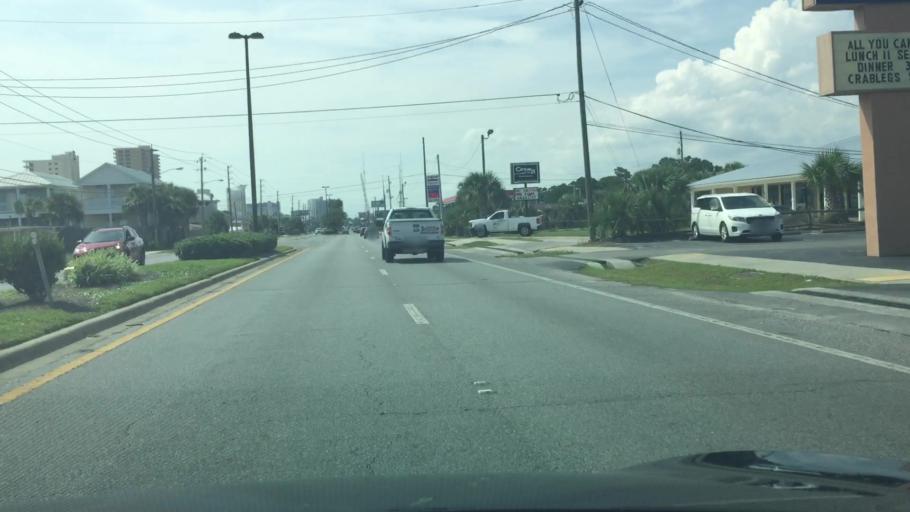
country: US
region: Florida
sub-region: Bay County
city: Panama City Beach
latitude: 30.1637
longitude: -85.7830
